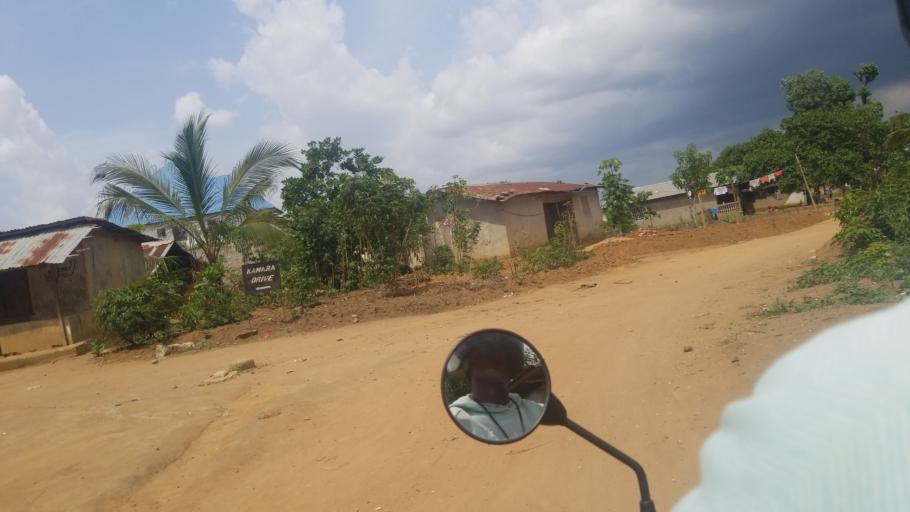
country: SL
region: Western Area
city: Waterloo
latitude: 8.3170
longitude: -13.0462
